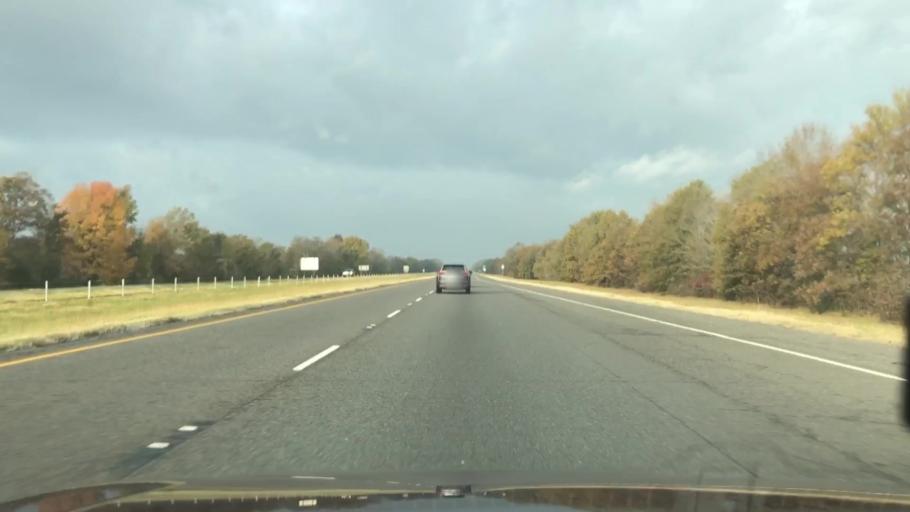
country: US
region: Louisiana
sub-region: Richland Parish
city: Delhi
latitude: 32.4326
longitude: -91.4258
